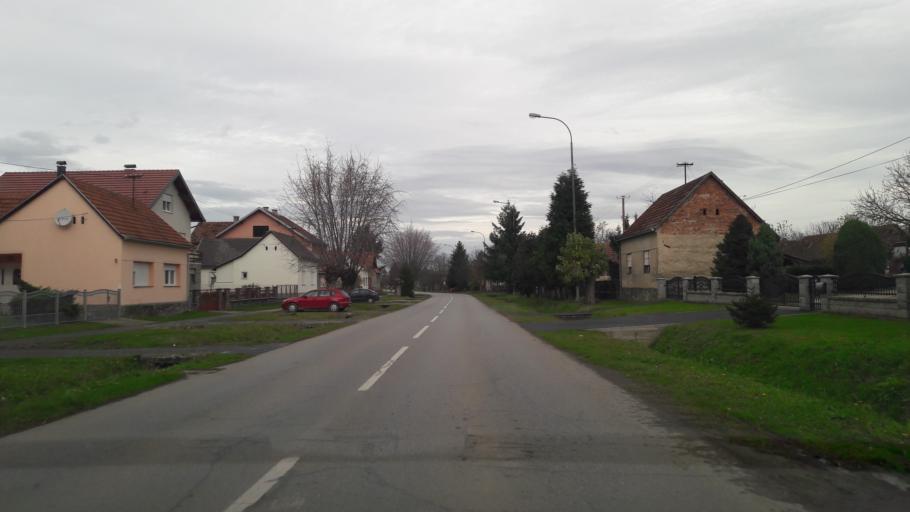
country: HR
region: Virovitick-Podravska
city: Orahovica
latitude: 45.5434
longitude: 17.8989
